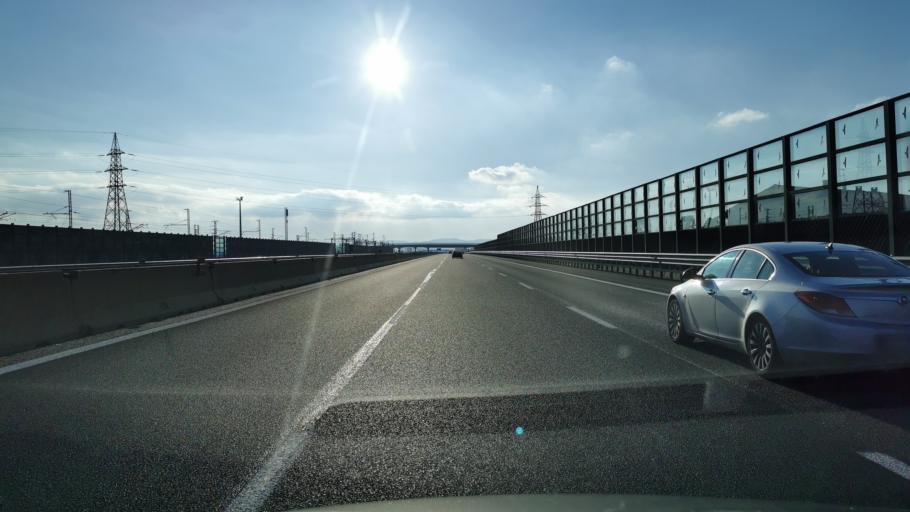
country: IT
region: Piedmont
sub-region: Provincia di Vercelli
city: Cigliano
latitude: 45.2834
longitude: 8.0316
